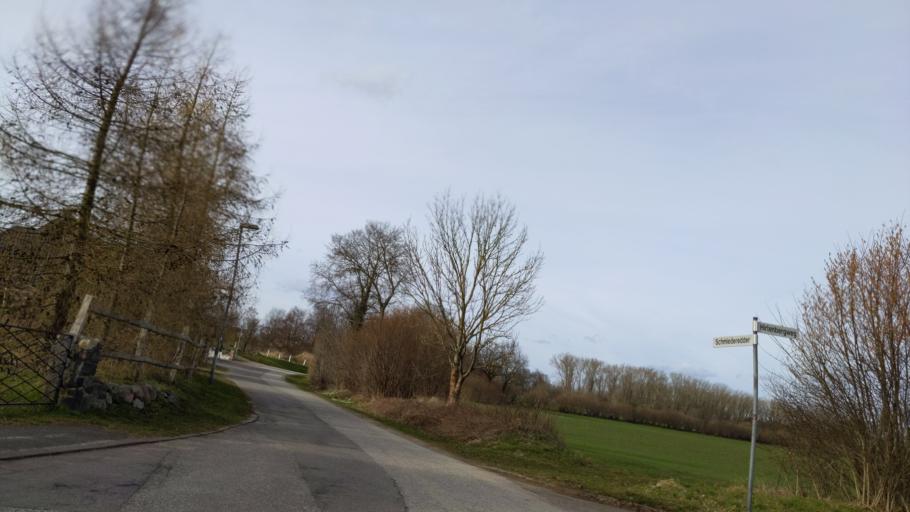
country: DE
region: Mecklenburg-Vorpommern
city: Selmsdorf
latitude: 53.9131
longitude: 10.8261
